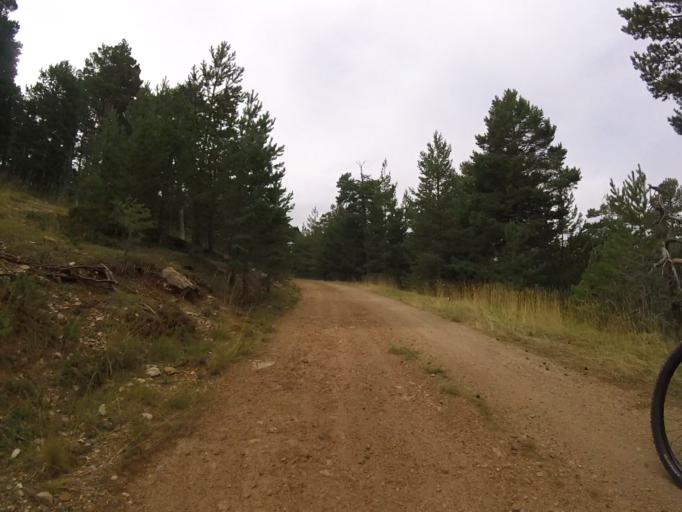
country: ES
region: Aragon
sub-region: Provincia de Teruel
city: Valdelinares
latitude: 40.3599
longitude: -0.6058
